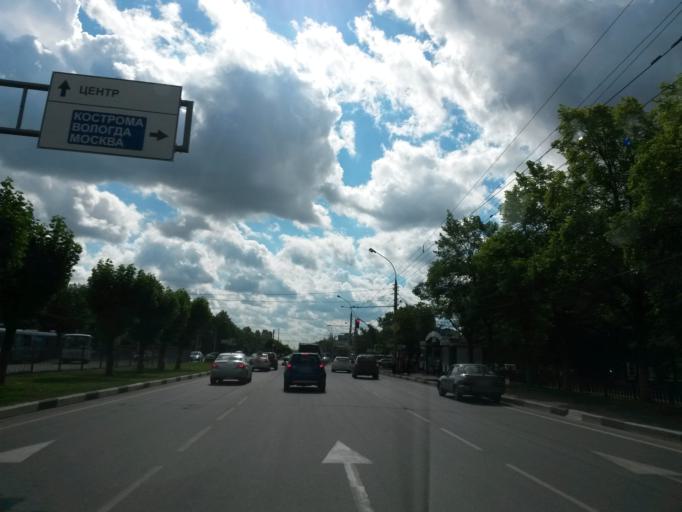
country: RU
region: Jaroslavl
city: Yaroslavl
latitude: 57.6864
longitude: 39.7834
